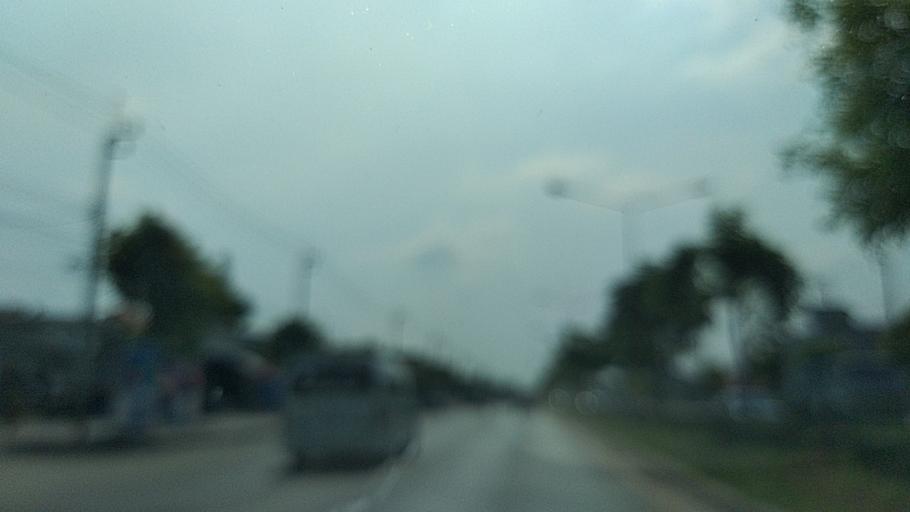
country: TH
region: Bangkok
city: Bang Khen
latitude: 13.8873
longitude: 100.6138
